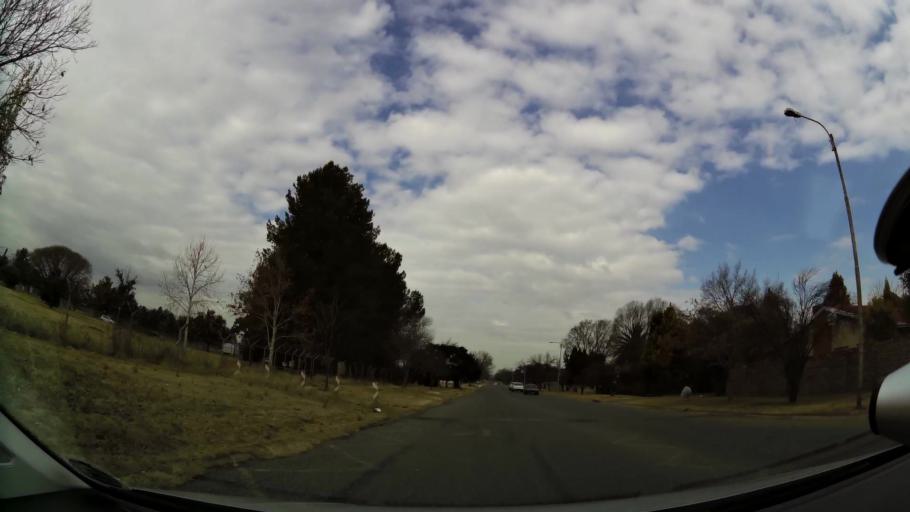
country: ZA
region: Orange Free State
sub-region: Fezile Dabi District Municipality
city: Kroonstad
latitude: -27.6426
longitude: 27.2387
